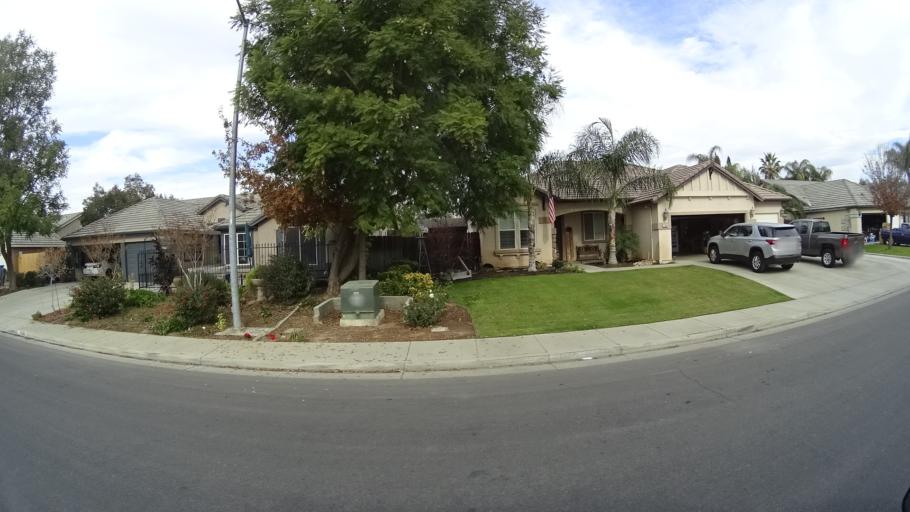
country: US
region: California
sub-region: Kern County
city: Rosedale
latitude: 35.4252
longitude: -119.1316
